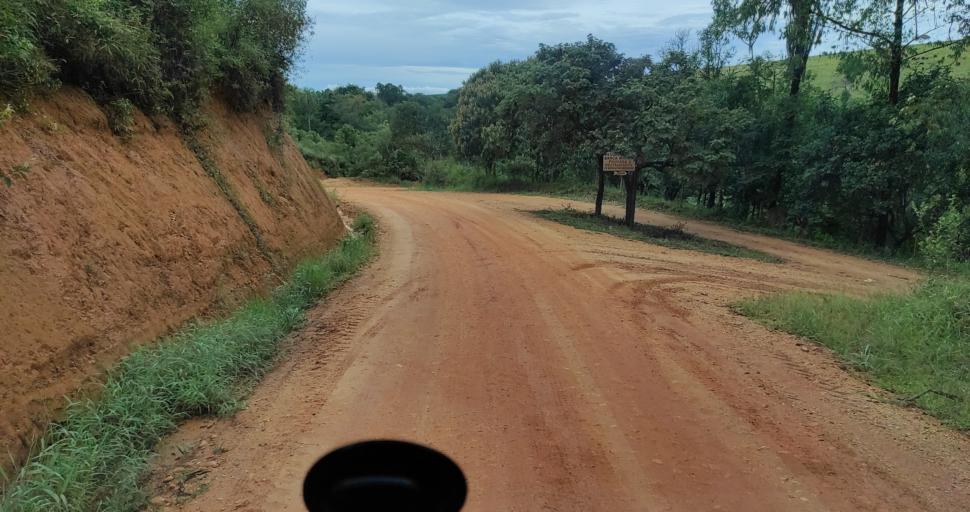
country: BR
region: Minas Gerais
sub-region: Piui
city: Piui
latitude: -20.2914
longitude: -46.3669
